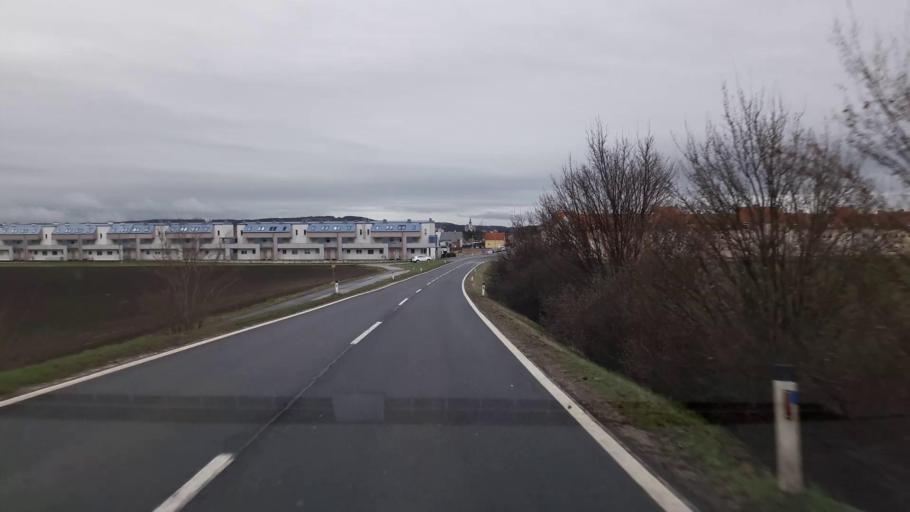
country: AT
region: Burgenland
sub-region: Politischer Bezirk Neusiedl am See
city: Bruckneudorf
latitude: 48.0403
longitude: 16.7855
